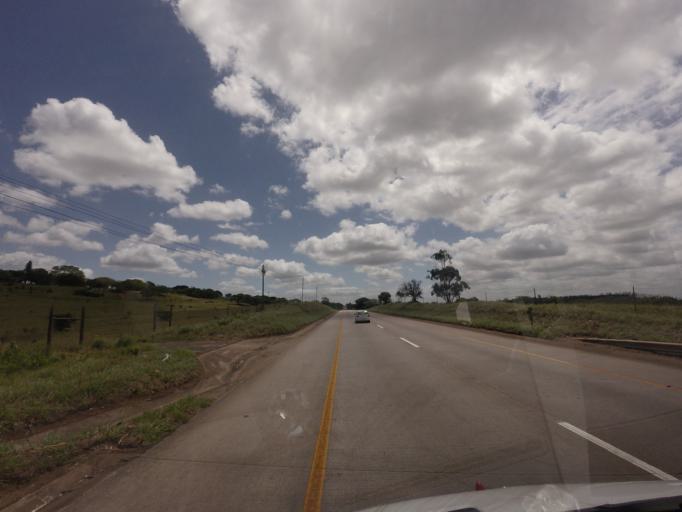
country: ZA
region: KwaZulu-Natal
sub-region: uMkhanyakude District Municipality
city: Mtubatuba
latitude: -28.4882
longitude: 32.1415
